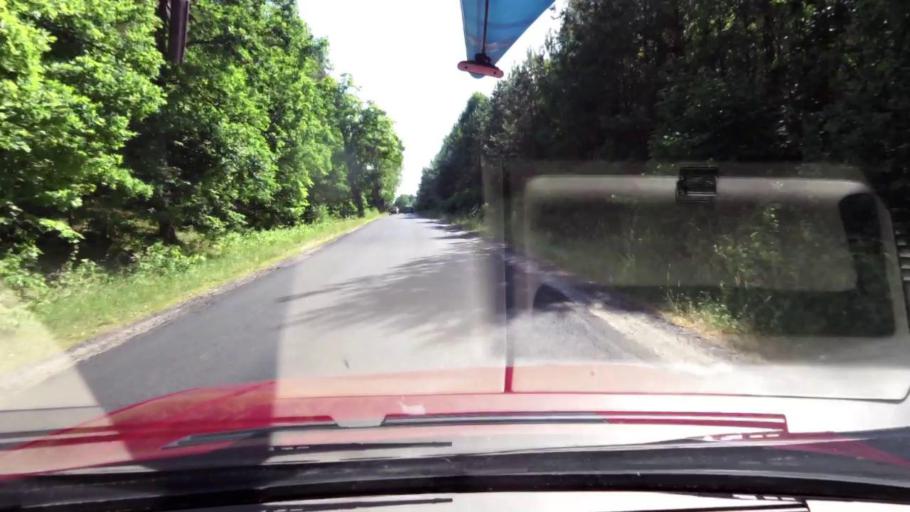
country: PL
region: Pomeranian Voivodeship
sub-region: Powiat slupski
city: Kepice
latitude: 54.2877
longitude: 16.9595
